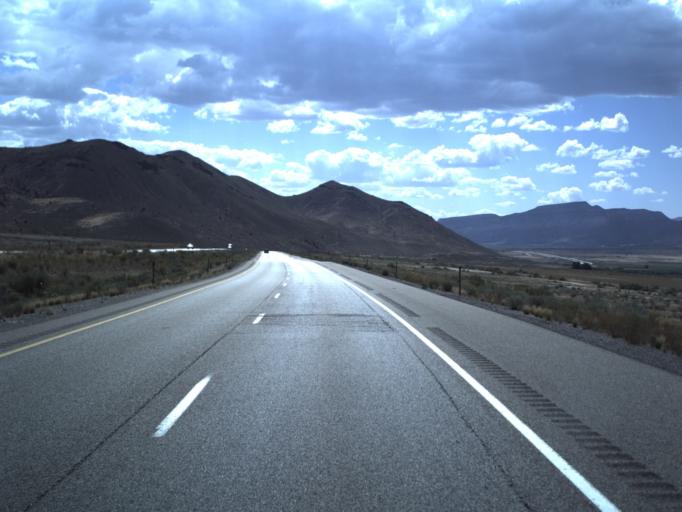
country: US
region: Utah
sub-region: Sevier County
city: Aurora
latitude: 38.8873
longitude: -111.9148
